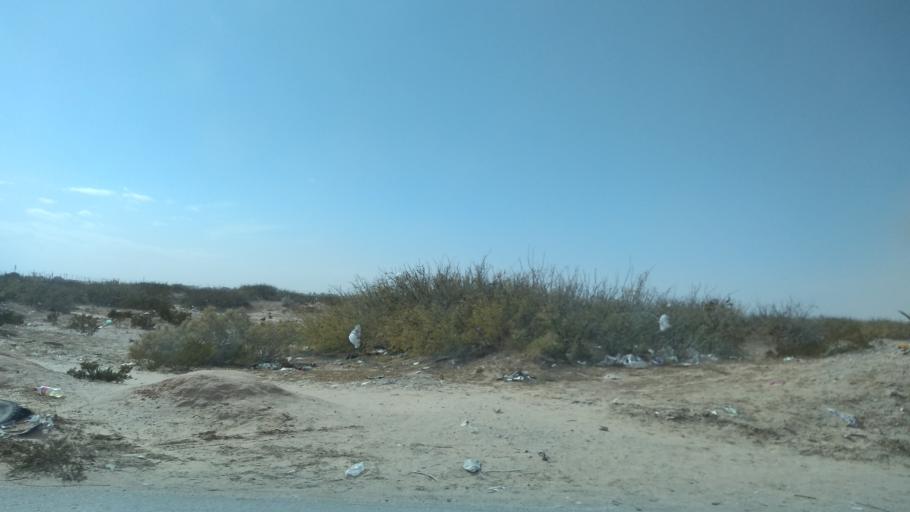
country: US
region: Texas
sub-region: El Paso County
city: San Elizario
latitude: 31.5746
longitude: -106.3304
